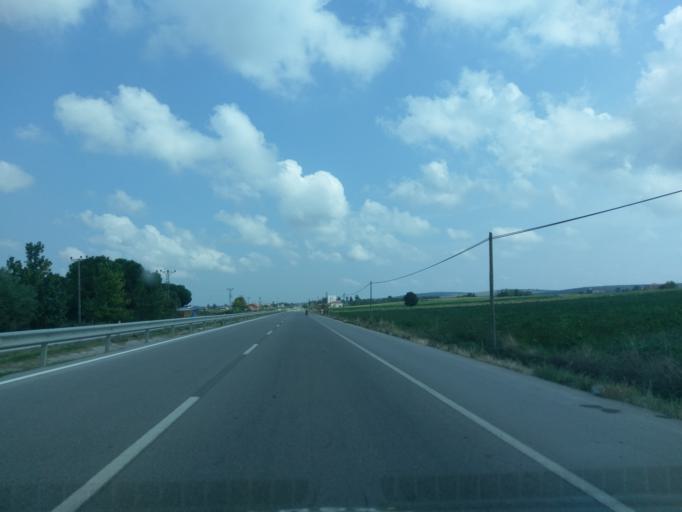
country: TR
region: Samsun
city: Bafra
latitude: 41.6014
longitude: 35.7945
